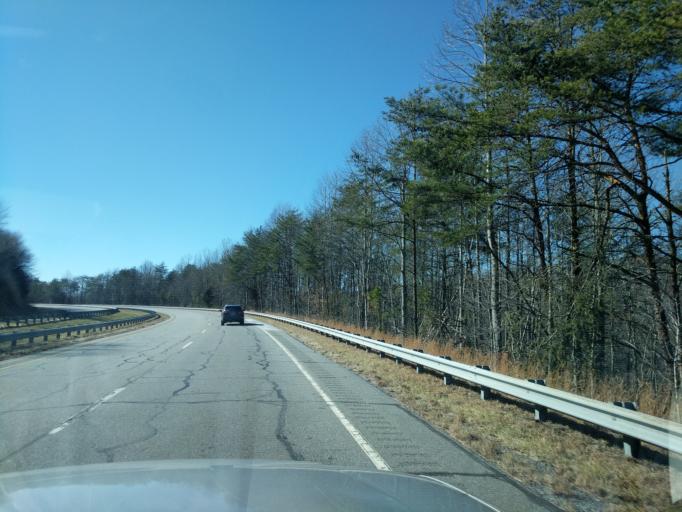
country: US
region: North Carolina
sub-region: Swain County
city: Bryson City
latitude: 35.4042
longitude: -83.4674
